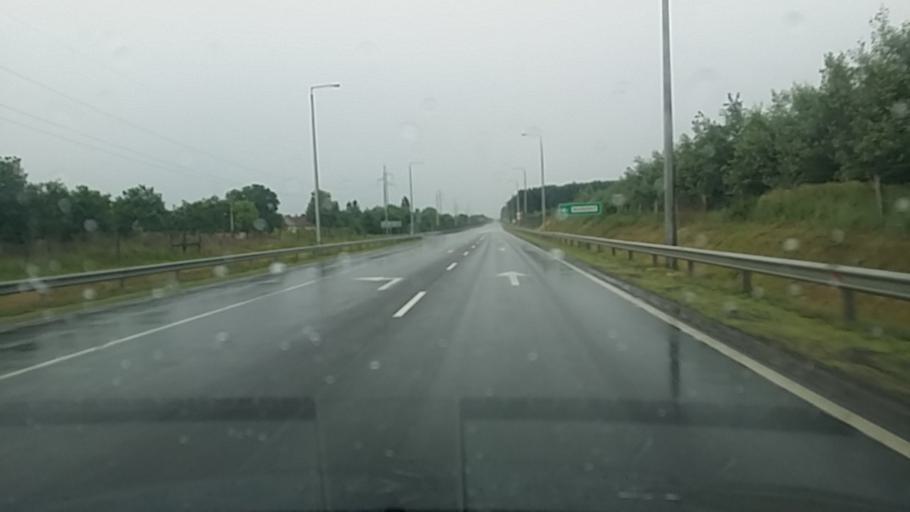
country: HU
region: Hajdu-Bihar
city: Hajduhadhaz
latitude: 47.6502
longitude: 21.6499
